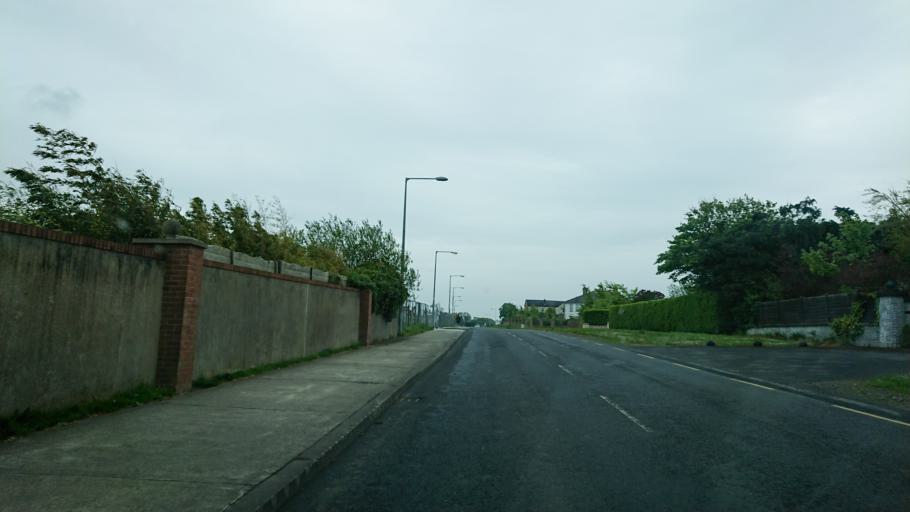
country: IE
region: Munster
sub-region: Waterford
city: Waterford
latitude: 52.2304
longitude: -7.0662
